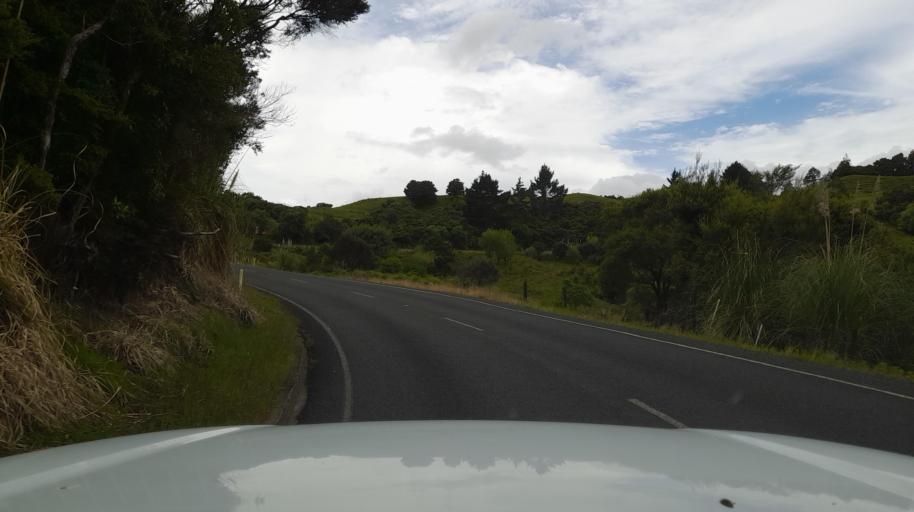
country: NZ
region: Northland
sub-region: Far North District
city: Kaitaia
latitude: -35.3620
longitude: 173.4006
